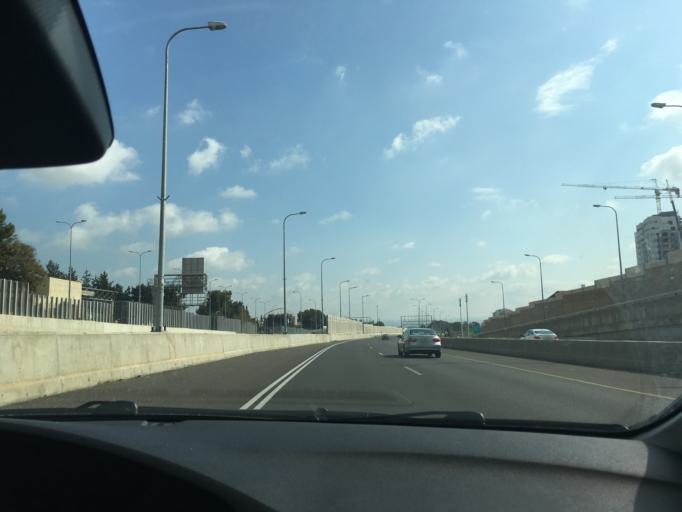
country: IL
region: Central District
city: Kfar Saba
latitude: 32.1723
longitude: 34.8952
